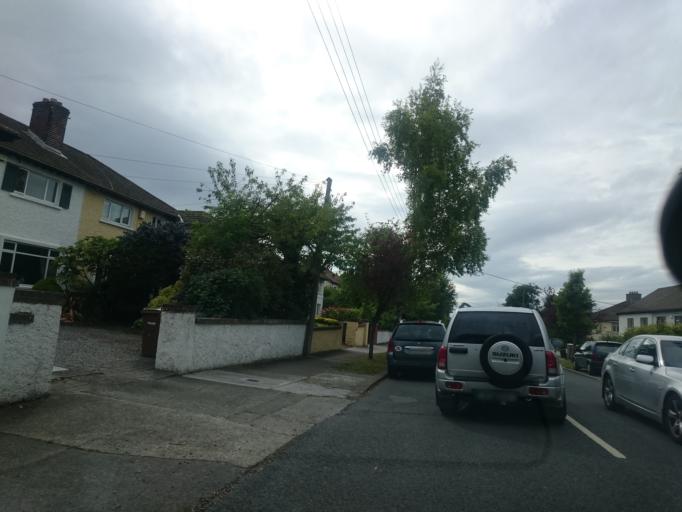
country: IE
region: Leinster
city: Mount Merrion
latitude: 53.2984
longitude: -6.2154
